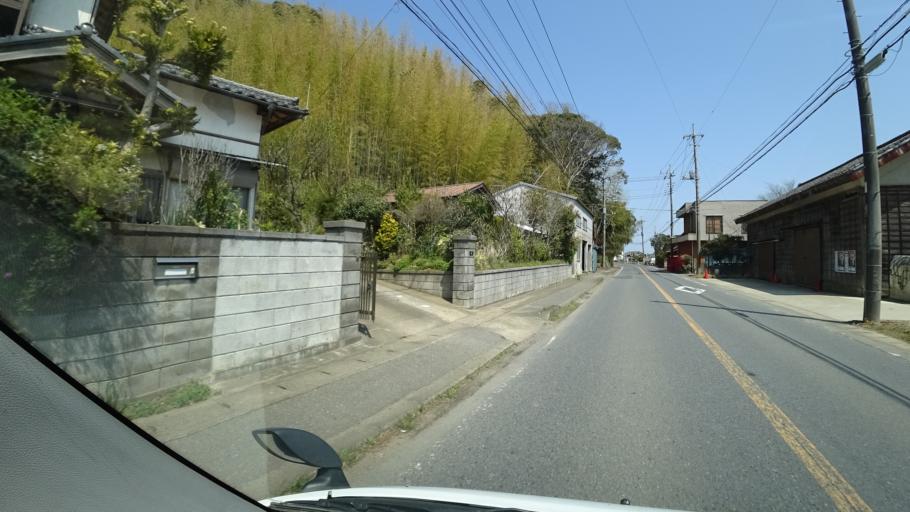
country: JP
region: Chiba
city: Yokaichiba
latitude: 35.7104
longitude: 140.4581
